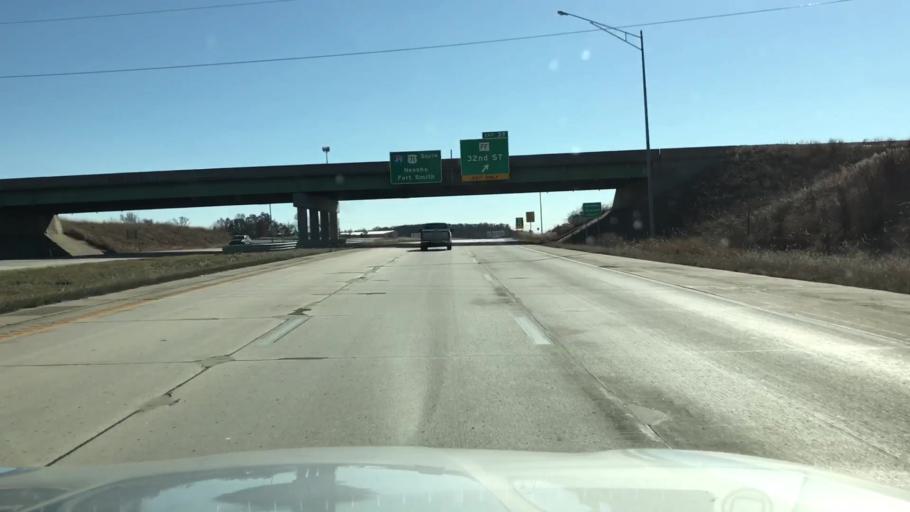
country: US
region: Missouri
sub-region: Jasper County
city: Duenweg
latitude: 37.0553
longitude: -94.4266
